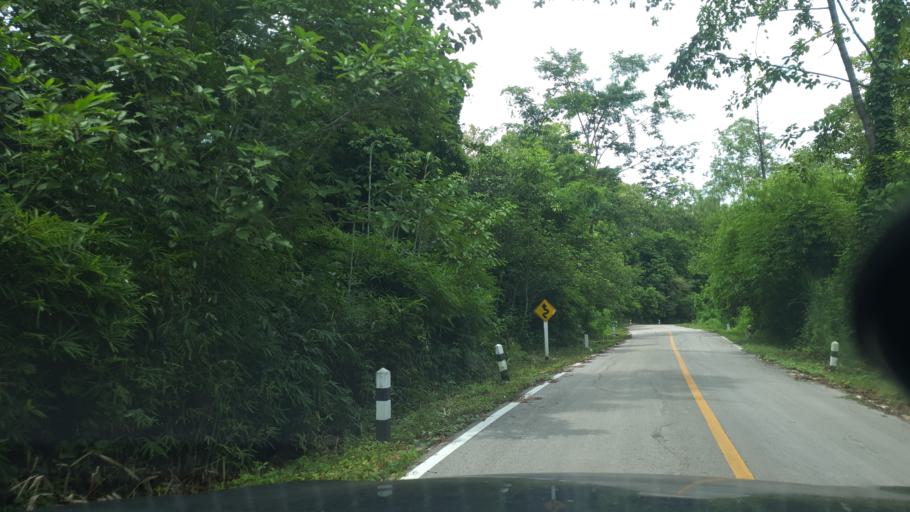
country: TH
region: Lampang
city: Hang Chat
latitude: 18.3824
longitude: 99.2591
